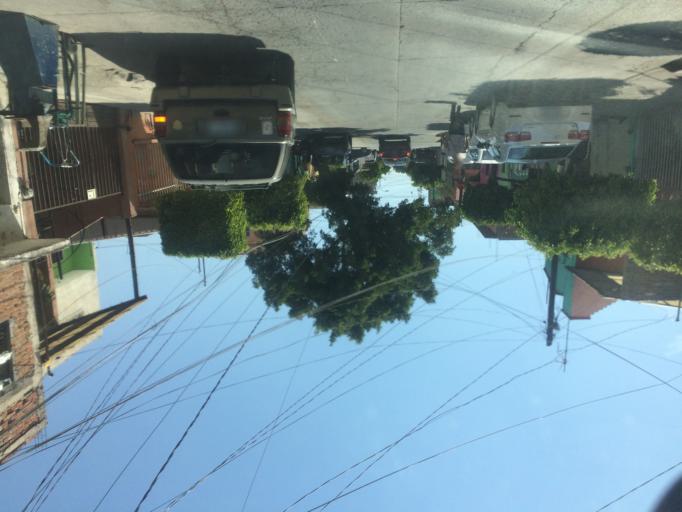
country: MX
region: Guanajuato
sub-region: Leon
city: La Ermita
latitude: 21.1353
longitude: -101.7052
